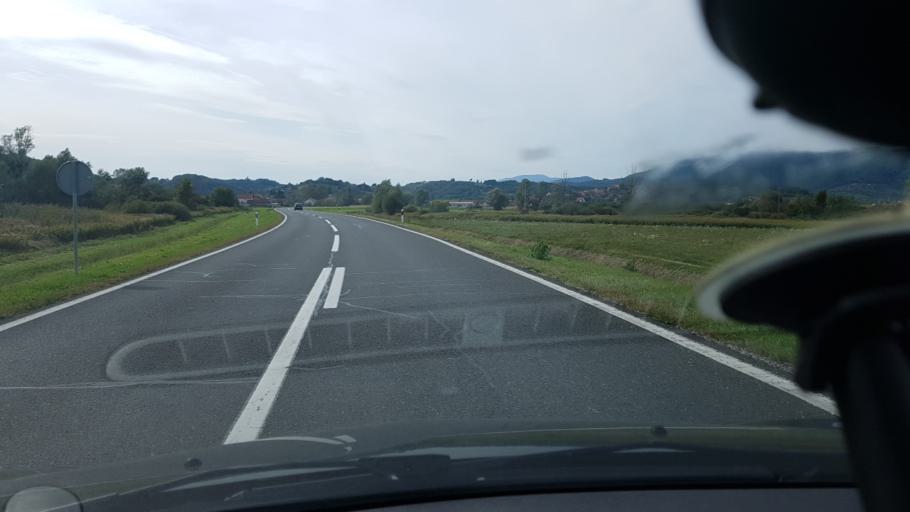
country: HR
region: Varazdinska
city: Remetinec
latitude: 46.1543
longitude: 16.3459
